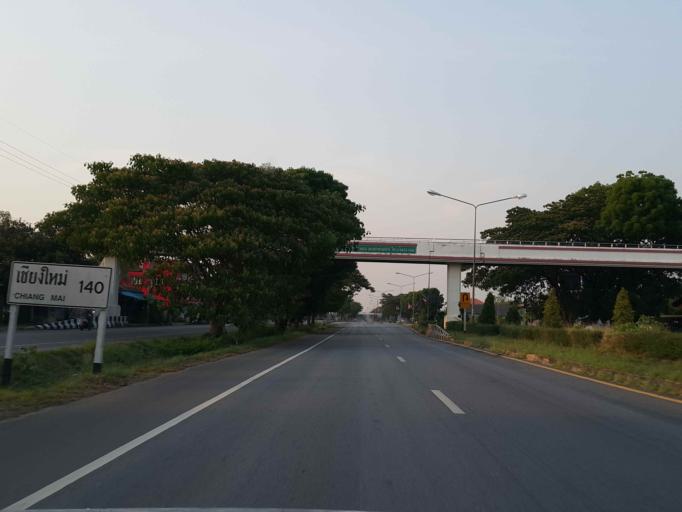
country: TH
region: Lampang
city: Sop Prap
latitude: 17.8847
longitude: 99.3385
